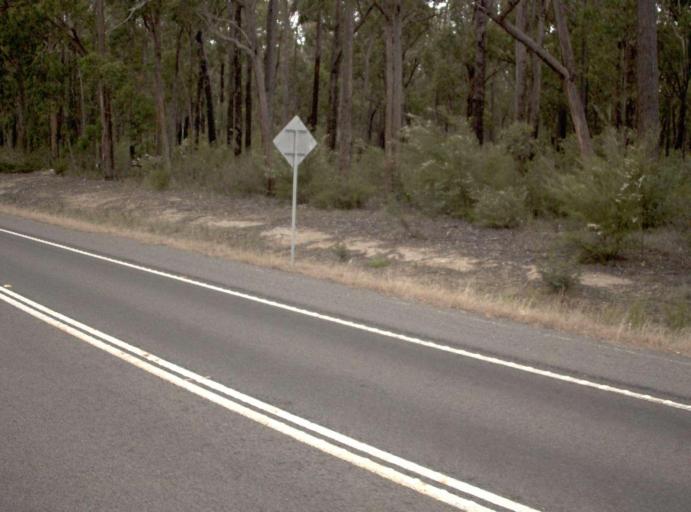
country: AU
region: Victoria
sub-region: East Gippsland
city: Lakes Entrance
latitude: -37.7272
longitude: 147.9490
